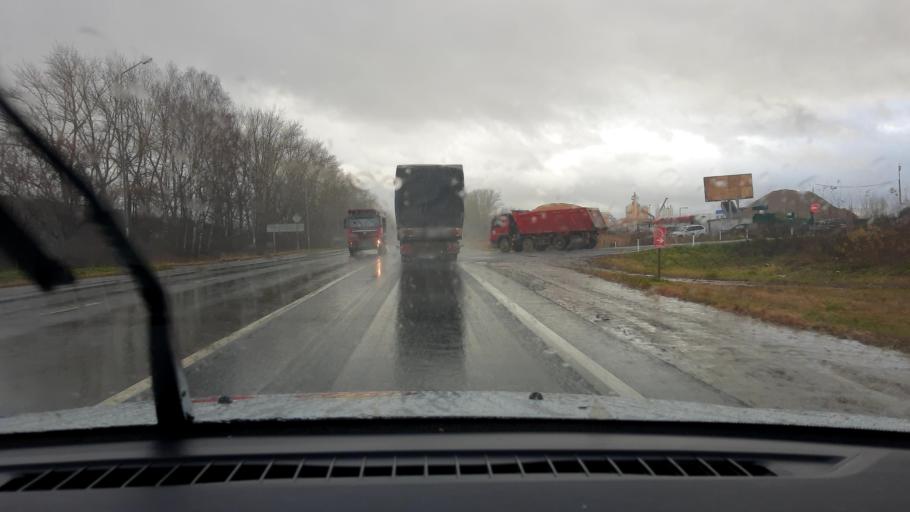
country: RU
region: Nizjnij Novgorod
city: Pamyat' Parizhskoy Kommuny
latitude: 56.0417
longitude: 44.4514
